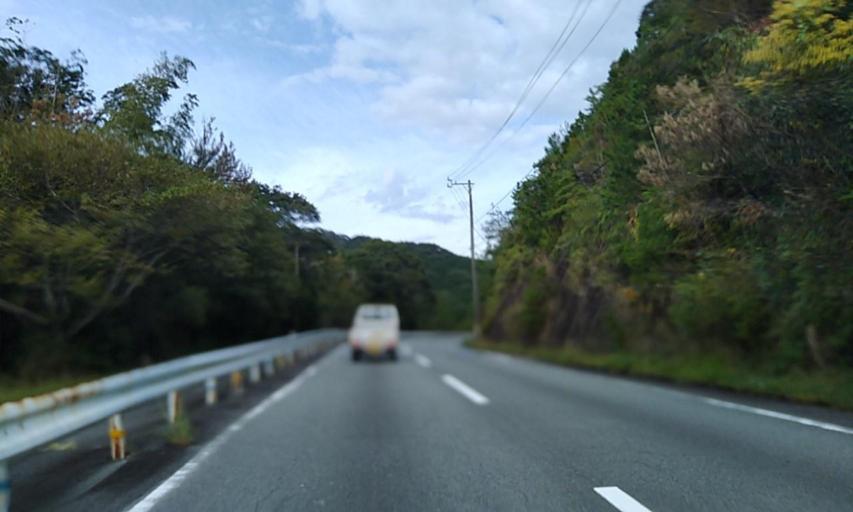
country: JP
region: Mie
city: Ise
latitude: 34.3002
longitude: 136.6043
